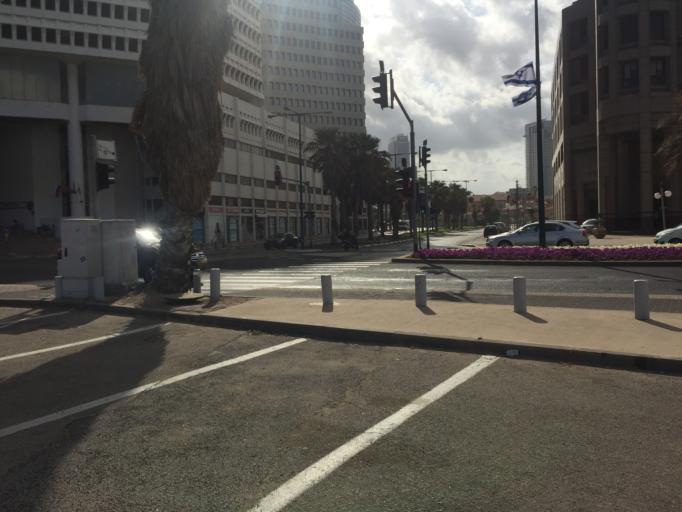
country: IL
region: Tel Aviv
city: Yafo
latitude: 32.0627
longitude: 34.7613
